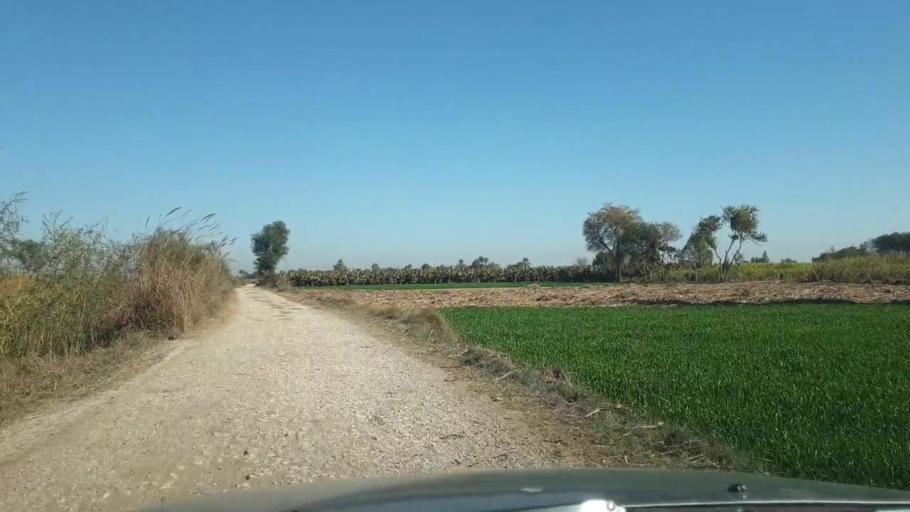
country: PK
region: Sindh
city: Ghotki
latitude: 28.0215
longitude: 69.2837
